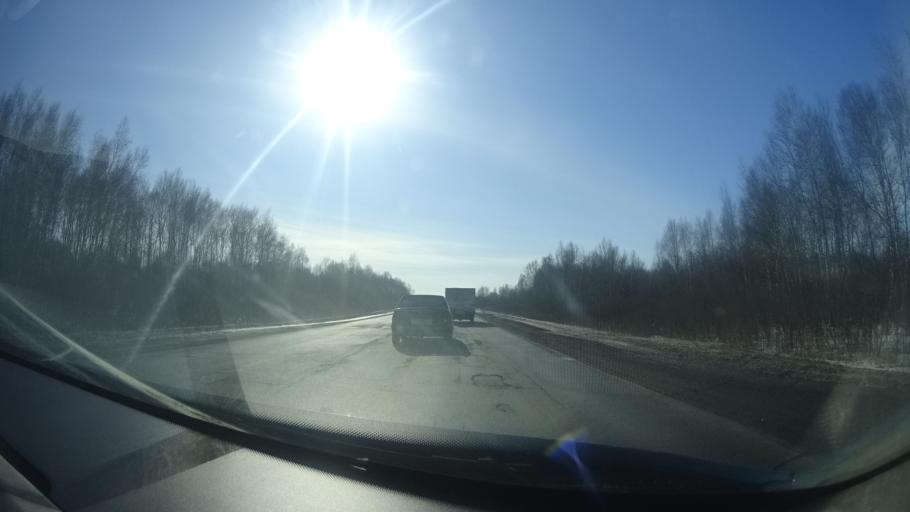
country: RU
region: Bashkortostan
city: Mikhaylovka
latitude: 54.9029
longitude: 55.7277
